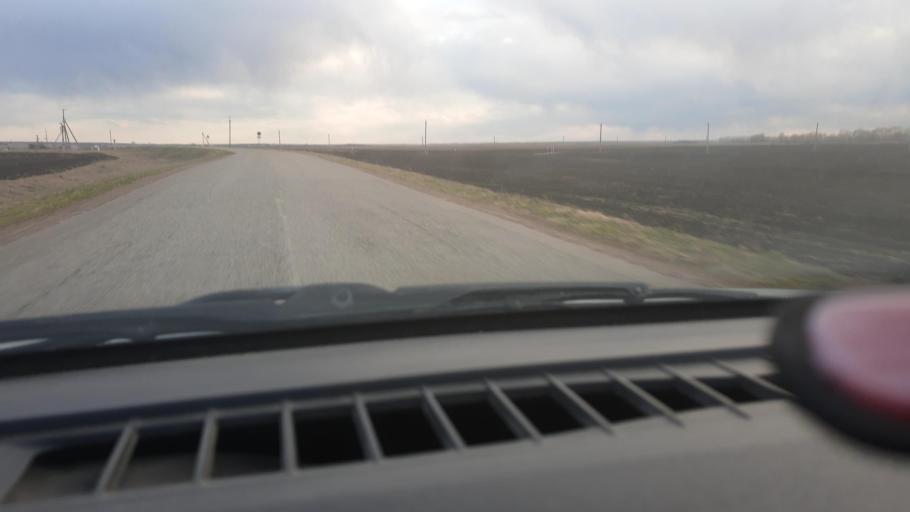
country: RU
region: Bashkortostan
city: Asanovo
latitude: 54.9417
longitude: 55.5182
